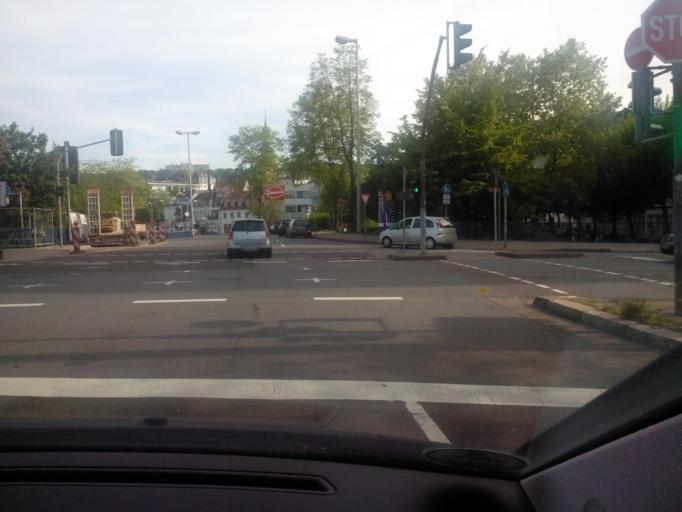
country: DE
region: Saarland
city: Saarbrucken
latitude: 49.2336
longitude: 6.9906
